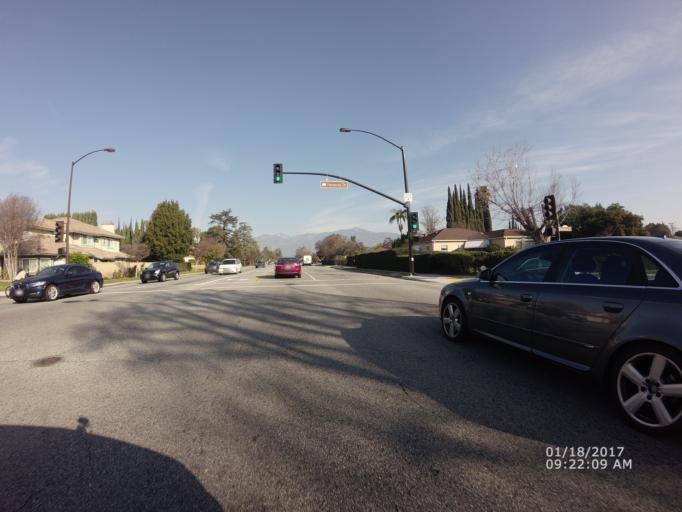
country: US
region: California
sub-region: Los Angeles County
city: East San Gabriel
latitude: 34.1062
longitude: -118.0910
